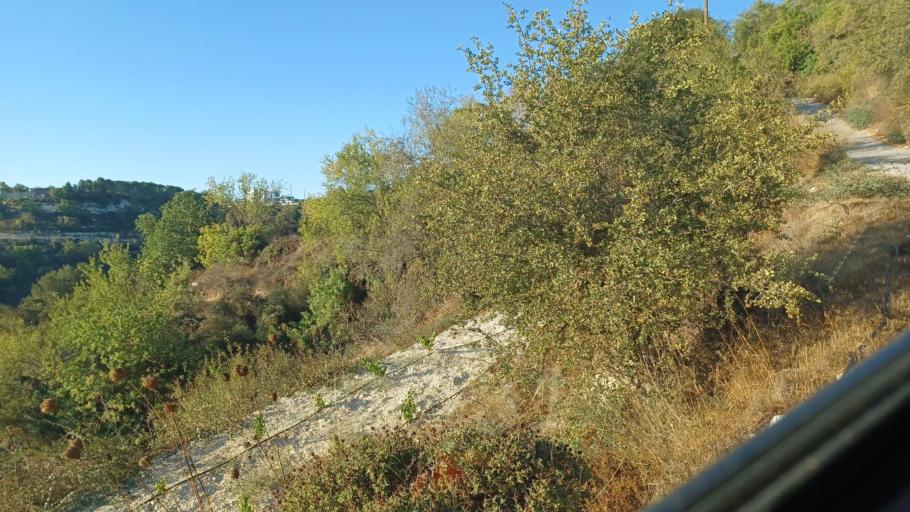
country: CY
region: Pafos
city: Tala
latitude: 34.8563
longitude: 32.4605
